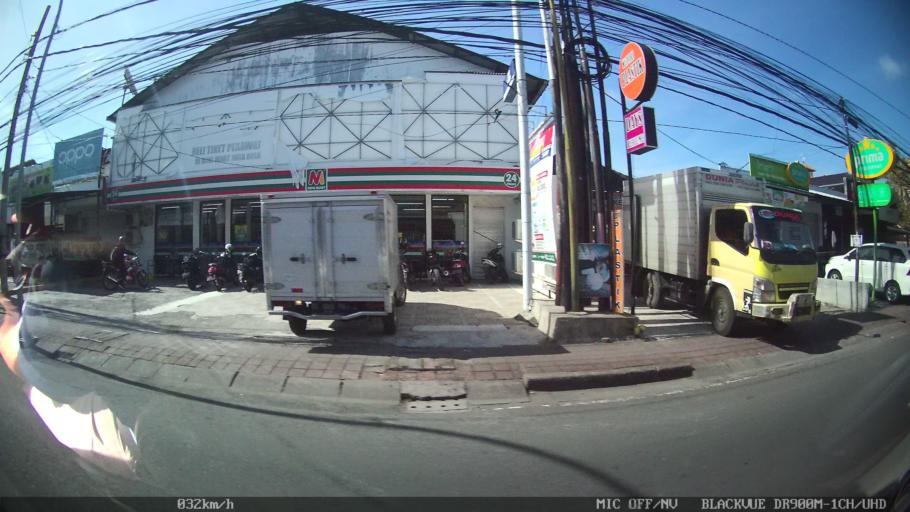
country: ID
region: Bali
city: Jabajero
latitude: -8.7380
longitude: 115.1712
